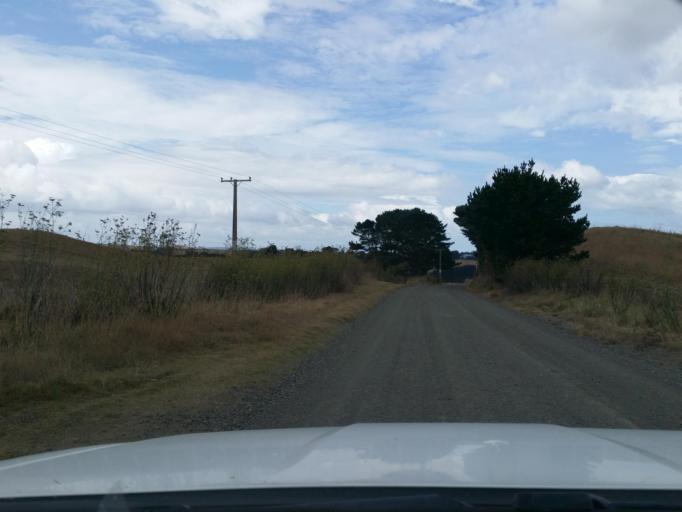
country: NZ
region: Auckland
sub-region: Auckland
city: Wellsford
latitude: -36.3197
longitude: 174.1346
